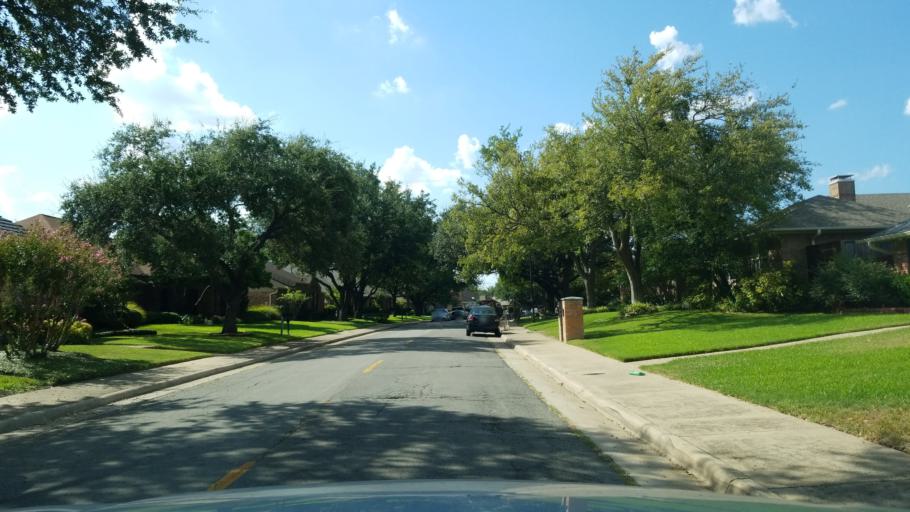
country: US
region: Texas
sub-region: Dallas County
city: Addison
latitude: 32.9702
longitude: -96.7953
